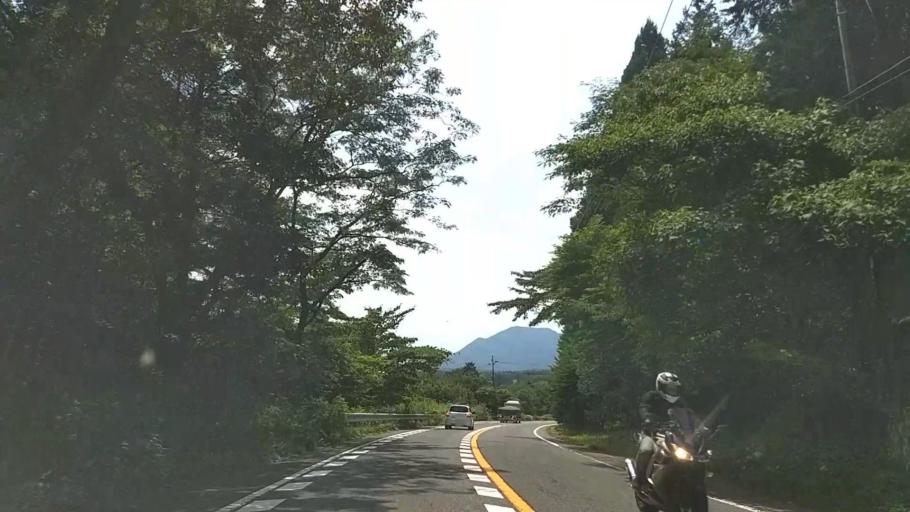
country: JP
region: Shizuoka
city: Fujinomiya
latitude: 35.3401
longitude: 138.5881
